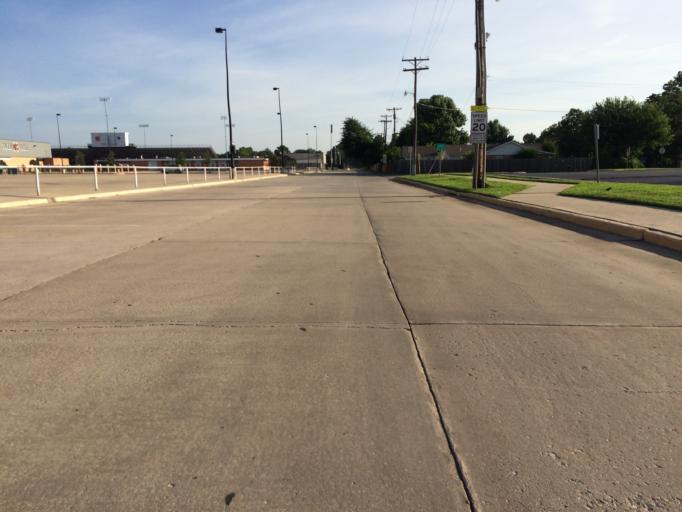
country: US
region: Oklahoma
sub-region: Cleveland County
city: Norman
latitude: 35.2186
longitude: -97.4546
